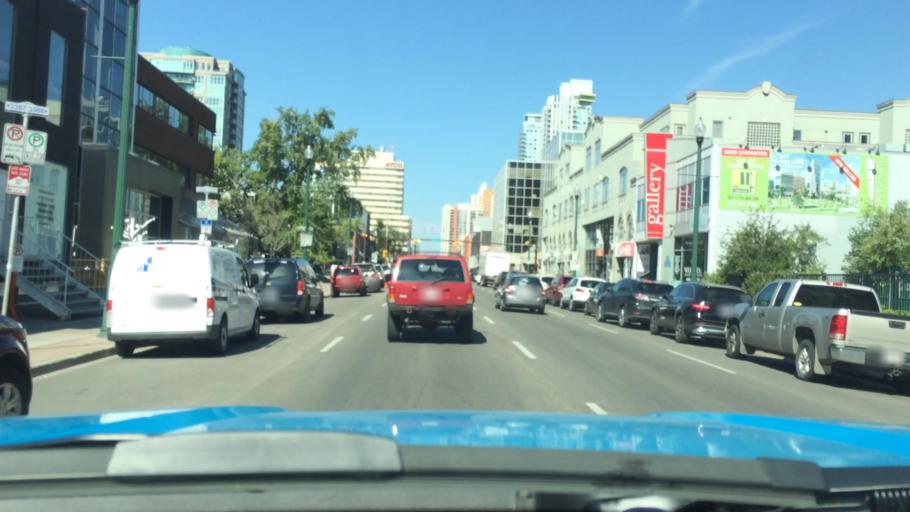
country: CA
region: Alberta
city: Calgary
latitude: 51.0427
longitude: -114.0751
